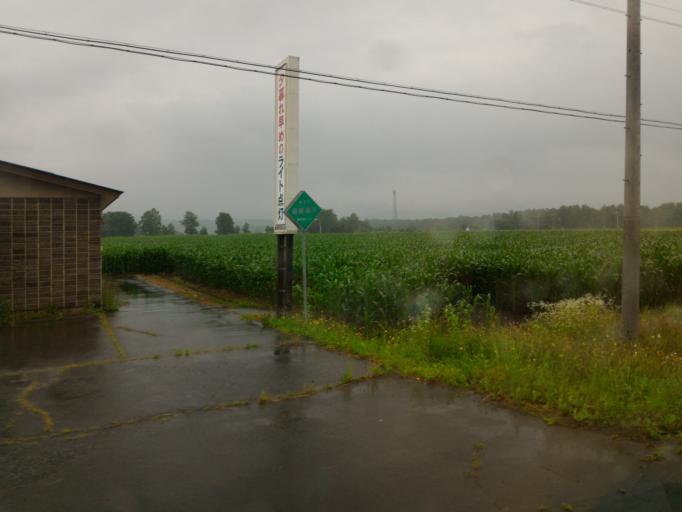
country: JP
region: Hokkaido
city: Nayoro
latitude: 44.5149
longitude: 142.3306
